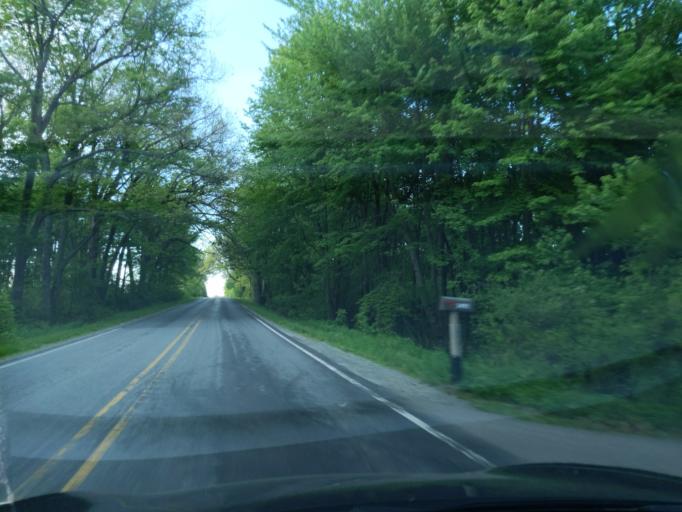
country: US
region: Michigan
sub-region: Ingham County
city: Leslie
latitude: 42.4829
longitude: -84.3170
